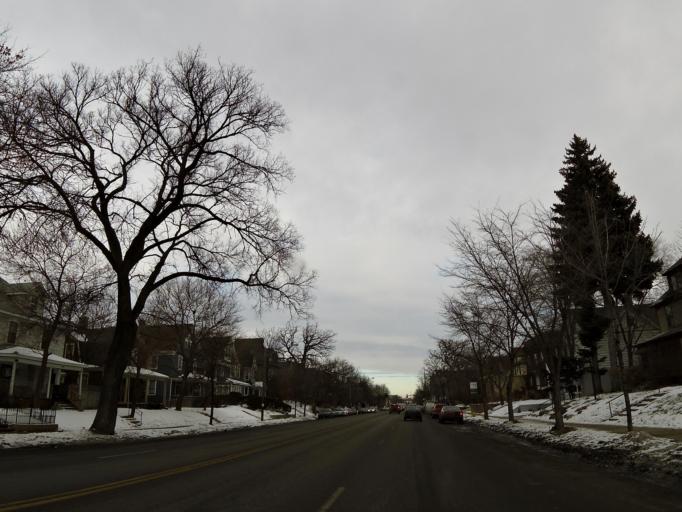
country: US
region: Minnesota
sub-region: Hennepin County
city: Minneapolis
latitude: 44.9574
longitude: -93.2880
